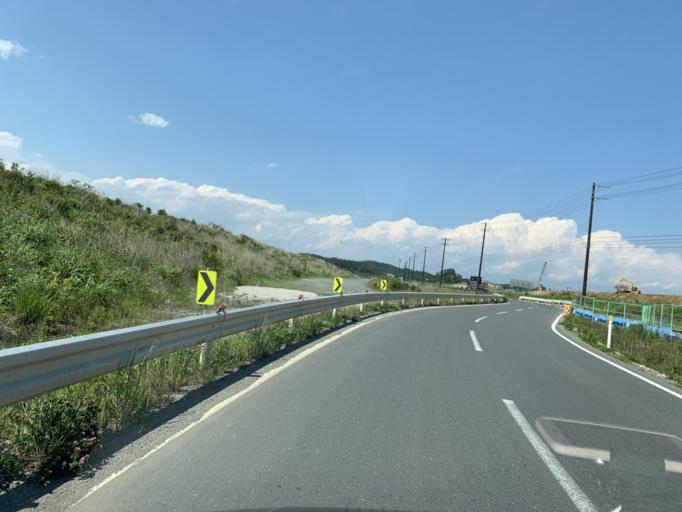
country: JP
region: Miyagi
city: Yamoto
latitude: 38.3605
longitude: 141.1559
